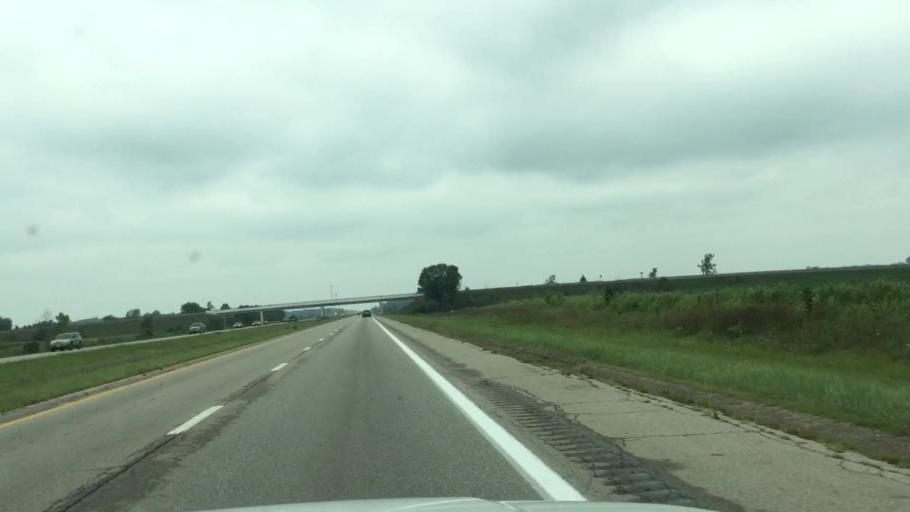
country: US
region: Ohio
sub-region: Union County
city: New California
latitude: 40.1860
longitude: -83.2568
